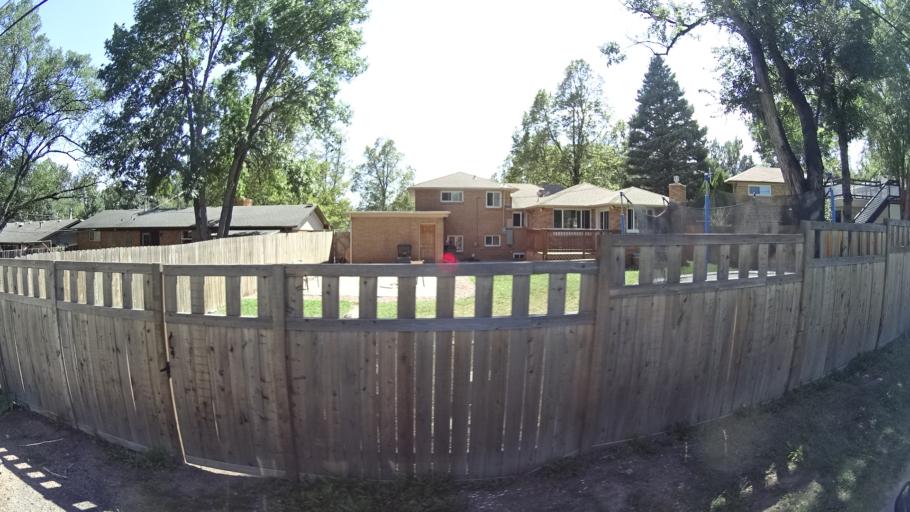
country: US
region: Colorado
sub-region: El Paso County
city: Manitou Springs
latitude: 38.8627
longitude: -104.8703
